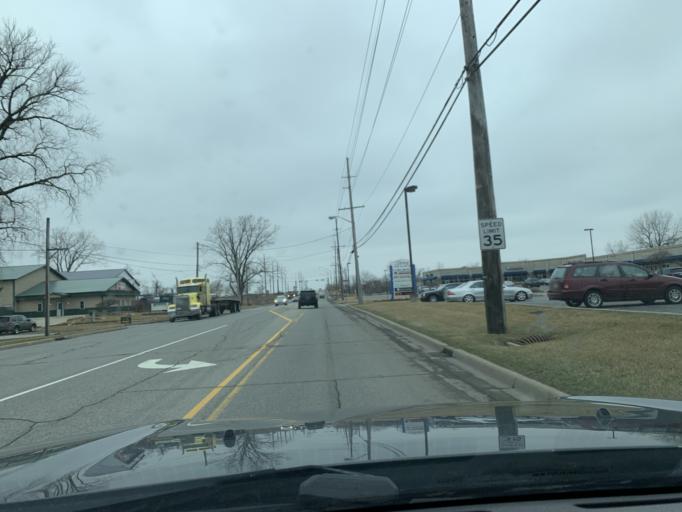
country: US
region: Indiana
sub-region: Lake County
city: Highland
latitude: 41.5231
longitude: -87.4627
